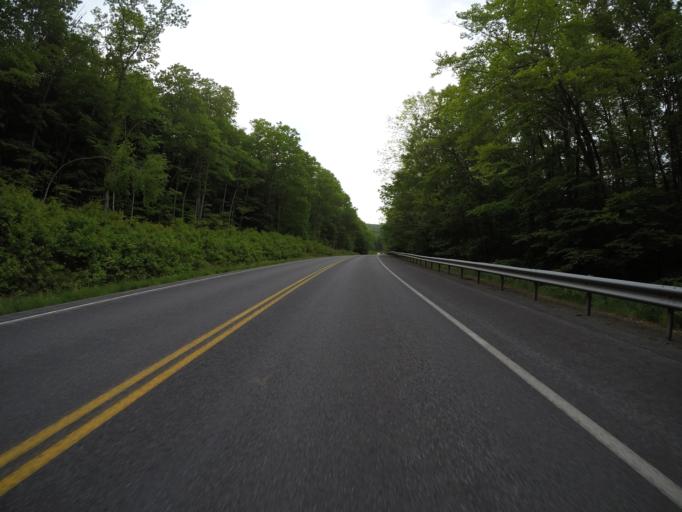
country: US
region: New York
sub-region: Sullivan County
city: Livingston Manor
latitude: 42.0597
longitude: -74.9224
